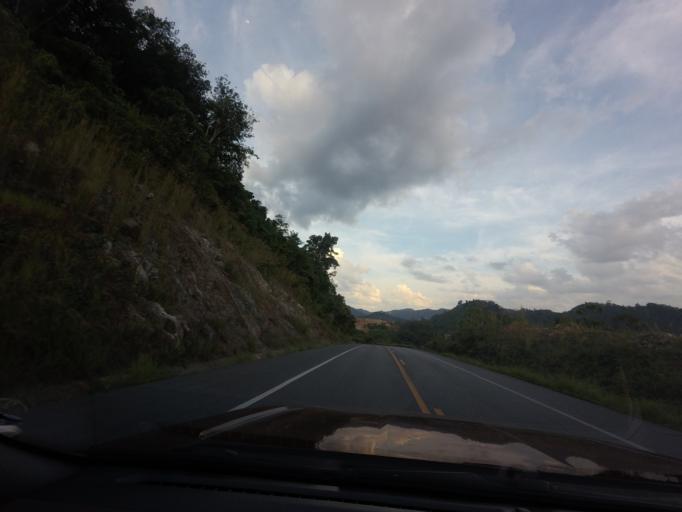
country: TH
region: Yala
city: Than To
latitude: 6.0530
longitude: 101.1945
